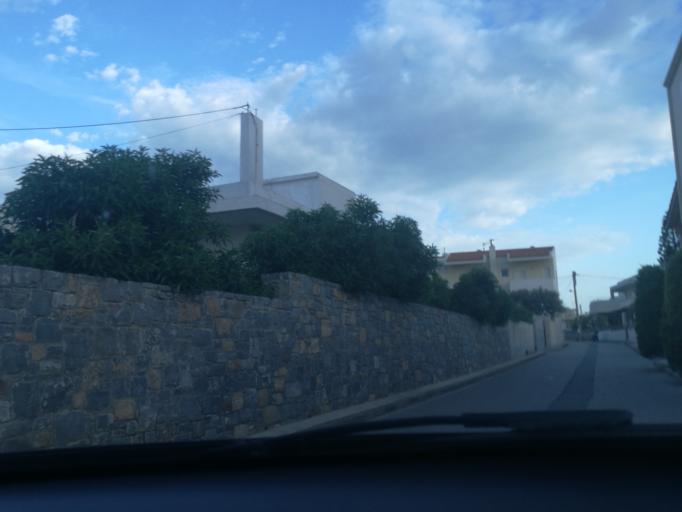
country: GR
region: Crete
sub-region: Nomos Irakleiou
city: Irakleion
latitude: 35.3179
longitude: 25.1472
